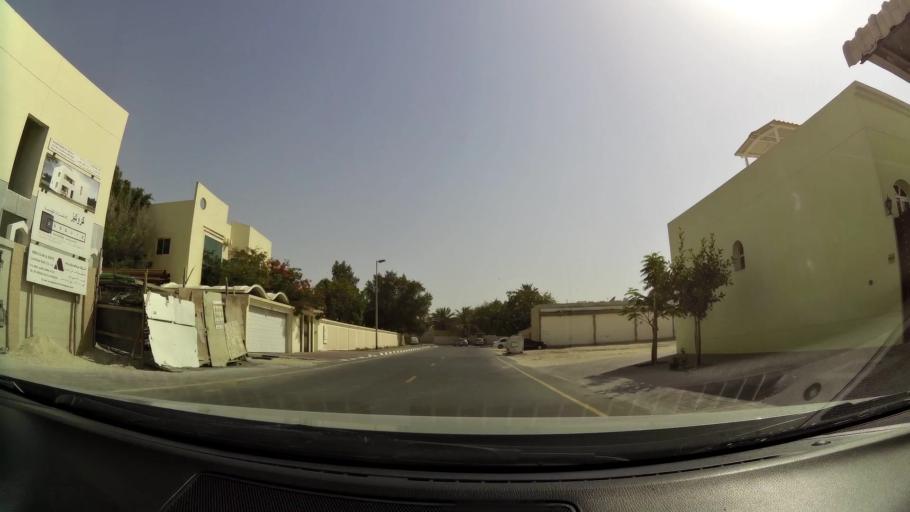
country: AE
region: Dubai
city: Dubai
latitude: 25.1668
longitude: 55.2536
